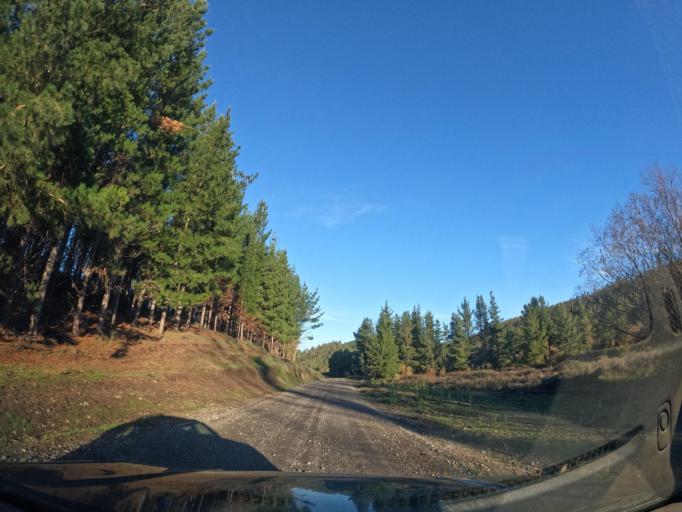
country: CL
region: Biobio
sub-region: Provincia de Concepcion
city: Chiguayante
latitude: -37.0925
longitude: -72.9011
